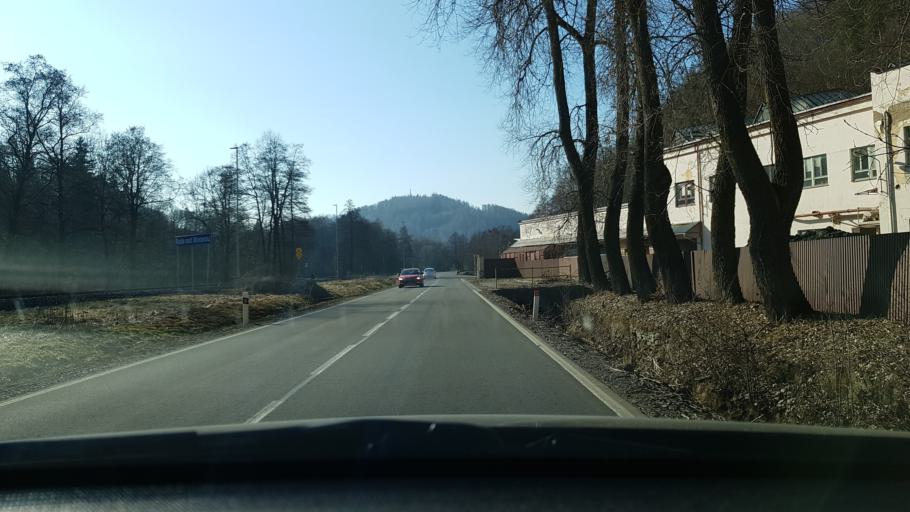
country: CZ
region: Olomoucky
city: Ruda nad Moravou
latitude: 49.9902
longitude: 16.8916
